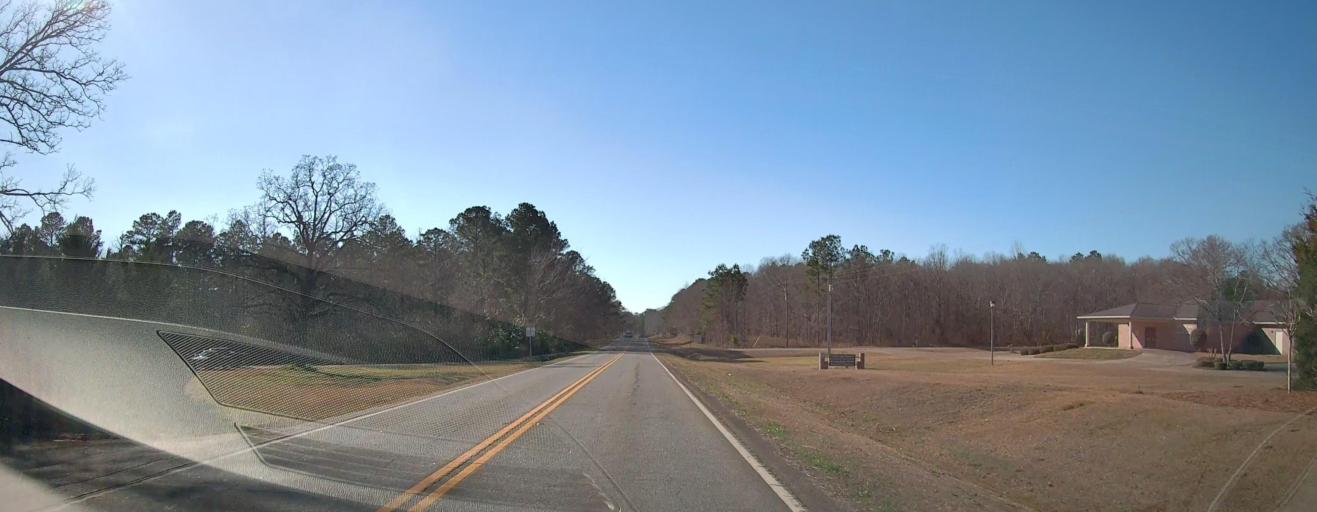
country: US
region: Georgia
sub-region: Sumter County
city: Americus
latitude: 32.0689
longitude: -84.1749
